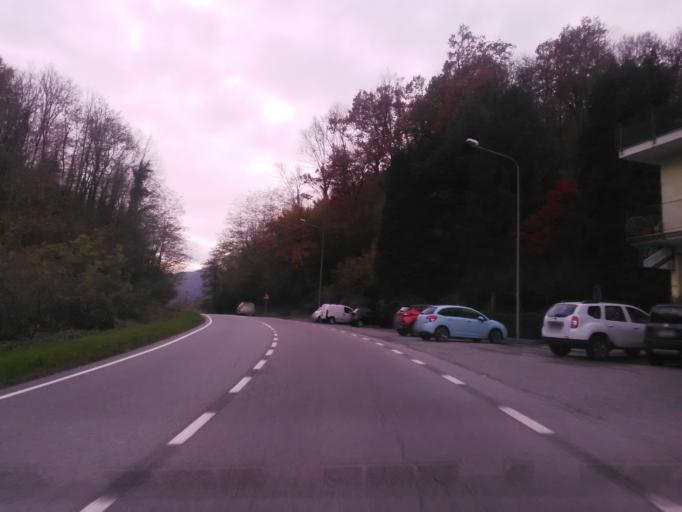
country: IT
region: Piedmont
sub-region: Provincia di Vercelli
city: Valduggia
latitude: 45.7191
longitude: 8.3019
